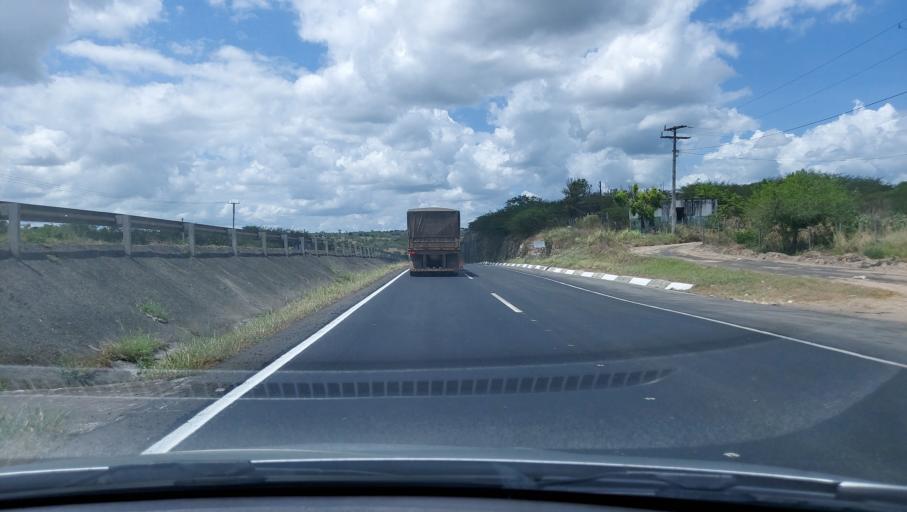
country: BR
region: Bahia
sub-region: Santo Estevao
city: Santo Estevao
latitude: -12.4264
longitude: -39.2071
